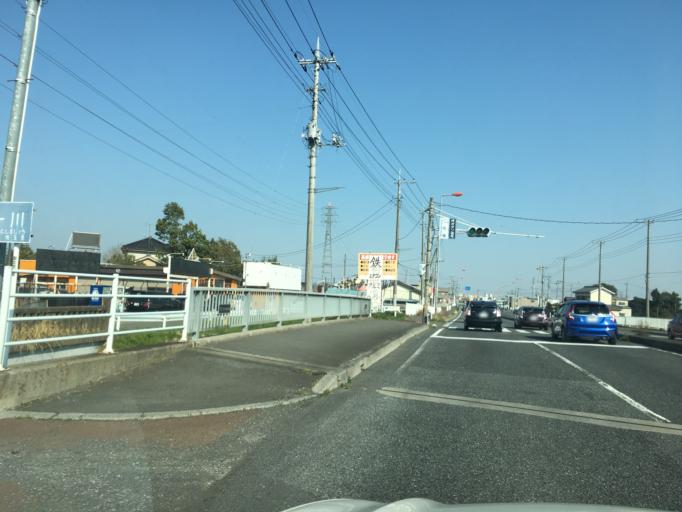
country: JP
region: Saitama
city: Kawagoe
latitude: 35.9192
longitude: 139.5095
